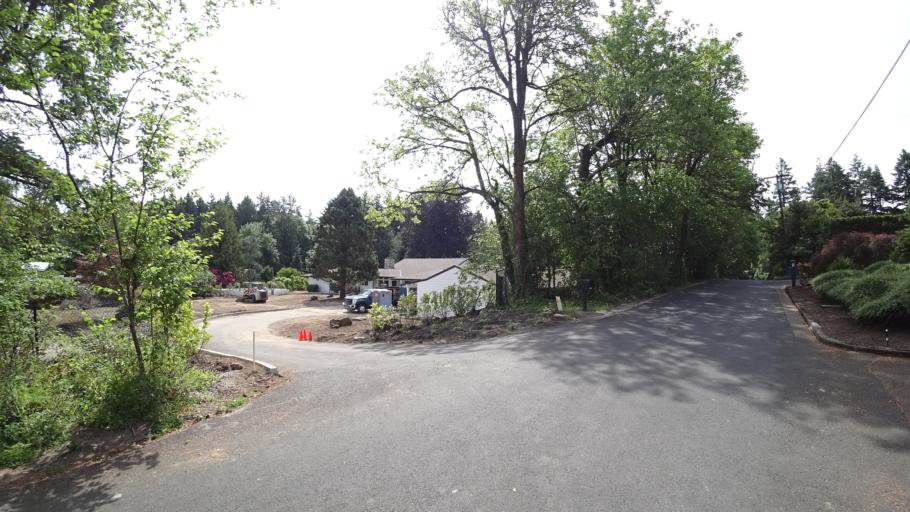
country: US
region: Oregon
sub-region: Clackamas County
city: Lake Oswego
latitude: 45.4423
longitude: -122.6645
